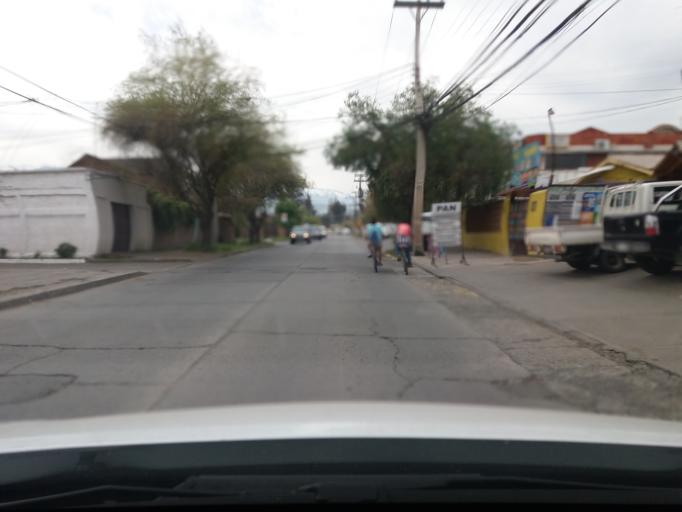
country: CL
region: Valparaiso
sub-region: Provincia de Los Andes
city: Los Andes
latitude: -32.8315
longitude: -70.6114
